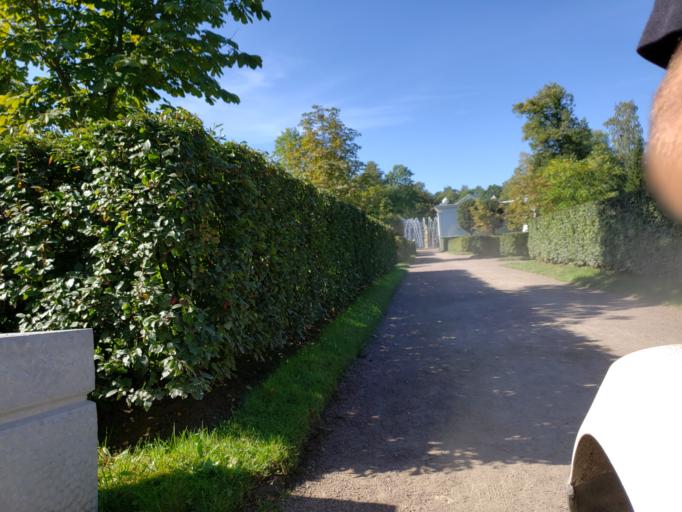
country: RU
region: St.-Petersburg
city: Peterhof
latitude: 59.8877
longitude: 29.9072
